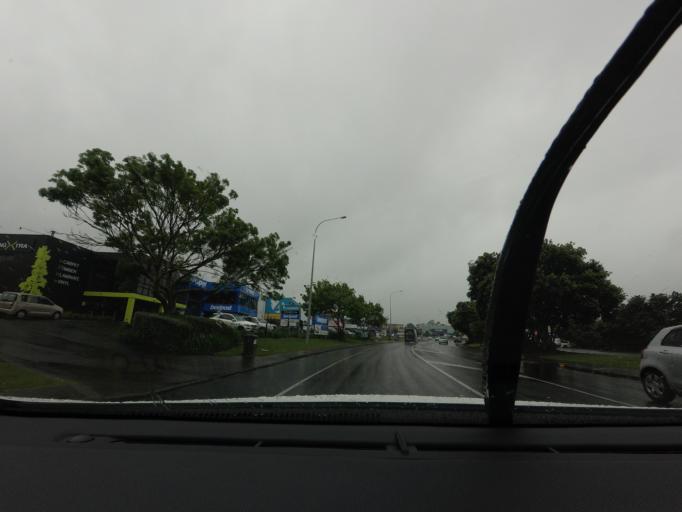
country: NZ
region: Auckland
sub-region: Auckland
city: North Shore
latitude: -36.7668
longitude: 174.7384
